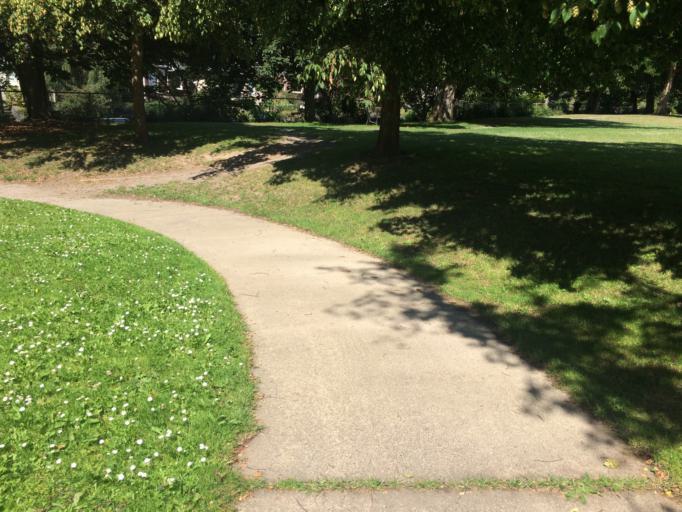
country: US
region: Washington
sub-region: King County
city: Seattle
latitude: 47.6647
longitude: -122.3334
